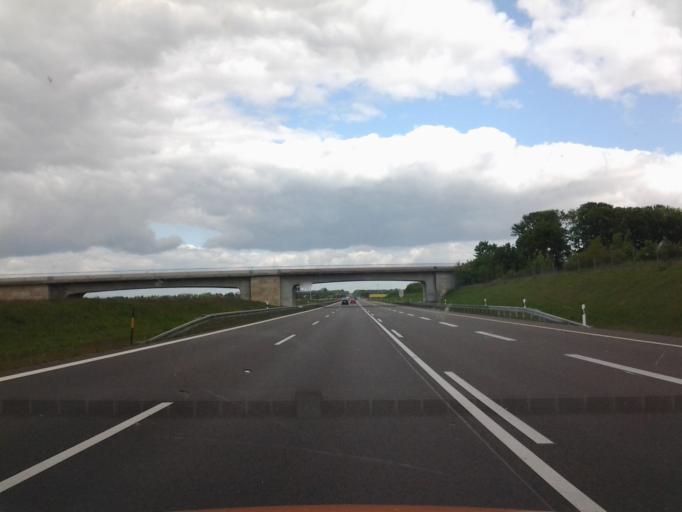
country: DE
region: Brandenburg
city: Ahrensfelde
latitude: 52.6240
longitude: 13.5639
